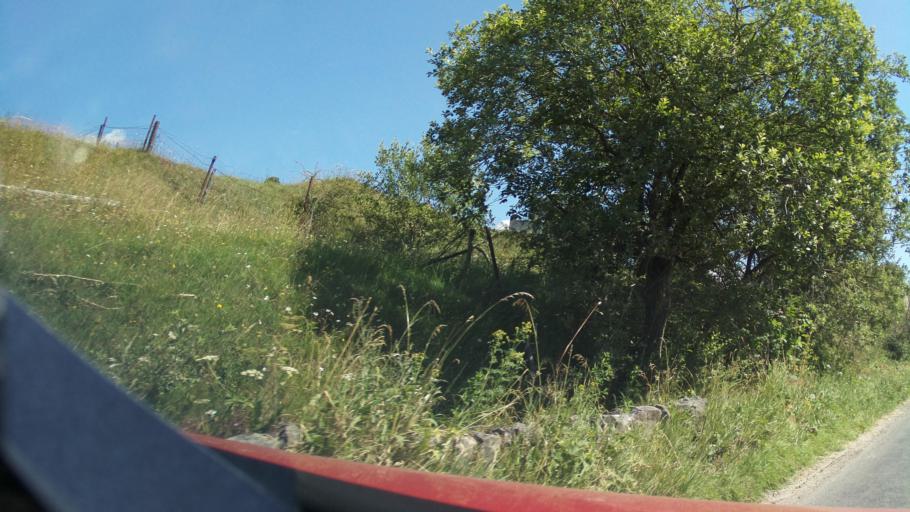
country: GB
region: England
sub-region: Derbyshire
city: Buxton
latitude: 53.2917
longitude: -1.8687
